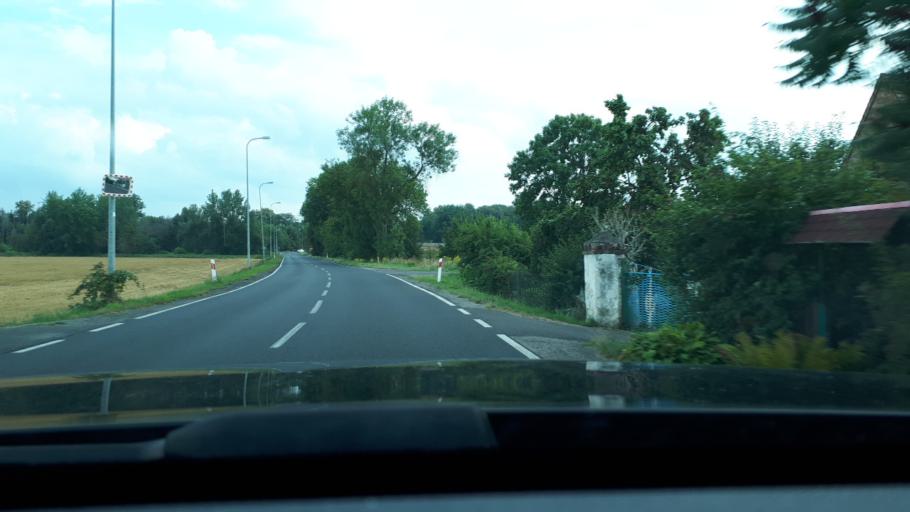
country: PL
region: Lower Silesian Voivodeship
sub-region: Powiat lubanski
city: Luban
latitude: 51.0789
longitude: 15.2952
